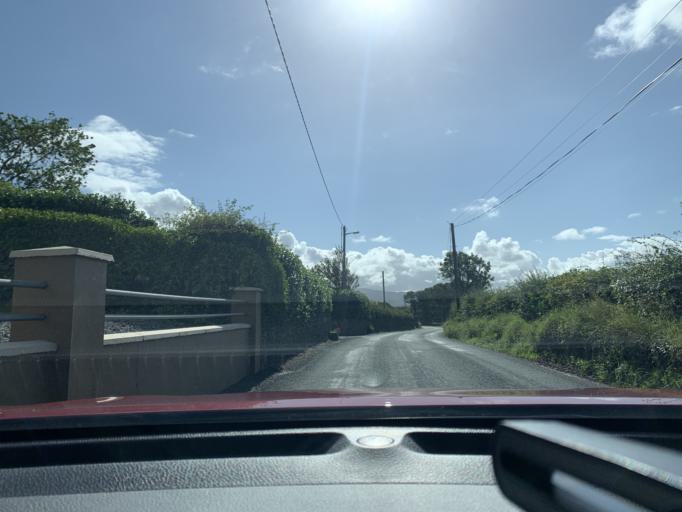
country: IE
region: Connaught
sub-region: Sligo
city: Strandhill
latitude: 54.3385
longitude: -8.5321
